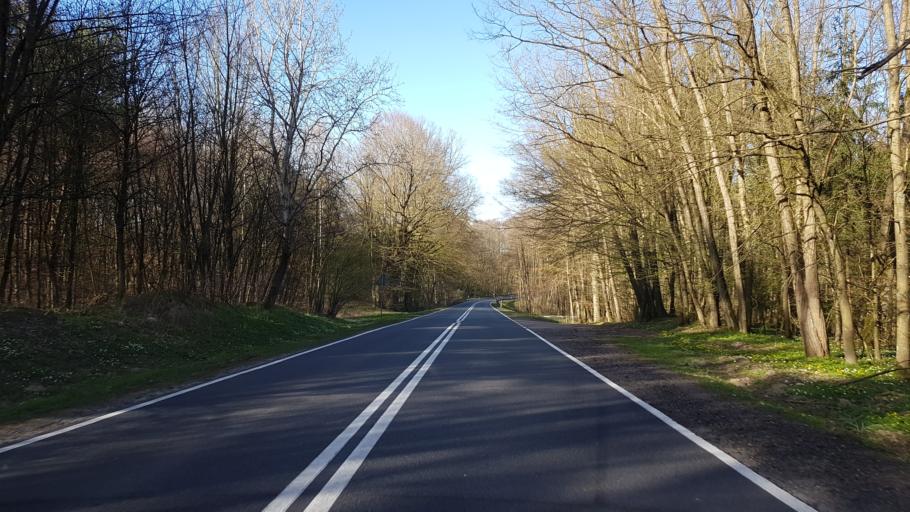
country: PL
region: West Pomeranian Voivodeship
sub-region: Powiat stargardzki
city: Chociwel
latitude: 53.5023
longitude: 15.4436
